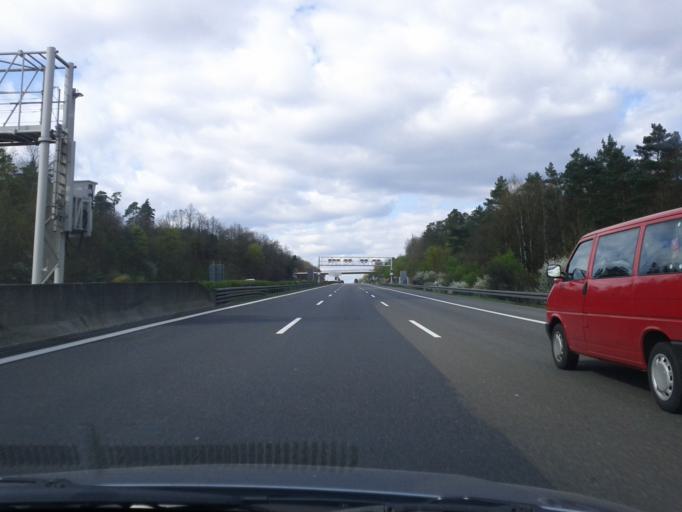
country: DE
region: Brandenburg
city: Grunheide
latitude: 52.4465
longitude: 13.8013
